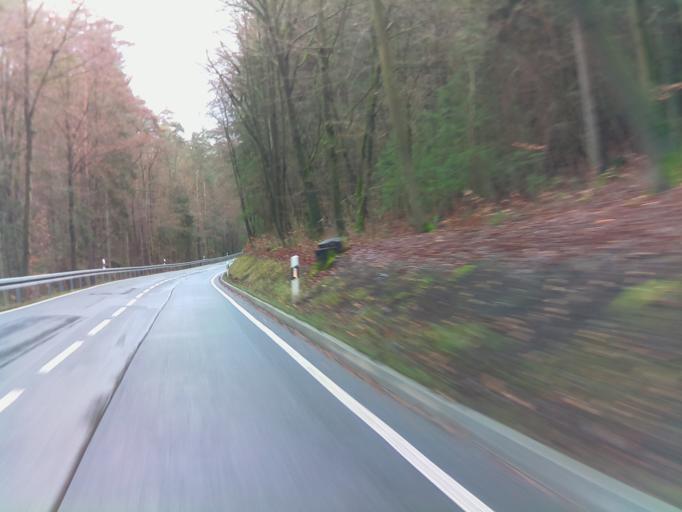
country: DE
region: Thuringia
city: Altenberga
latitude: 50.8532
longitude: 11.5342
